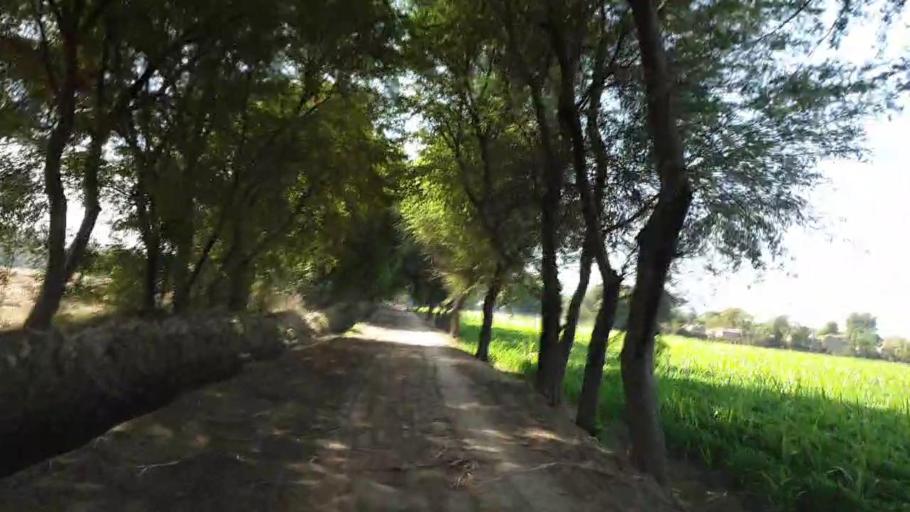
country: PK
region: Sindh
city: Matiari
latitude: 25.5313
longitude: 68.4873
